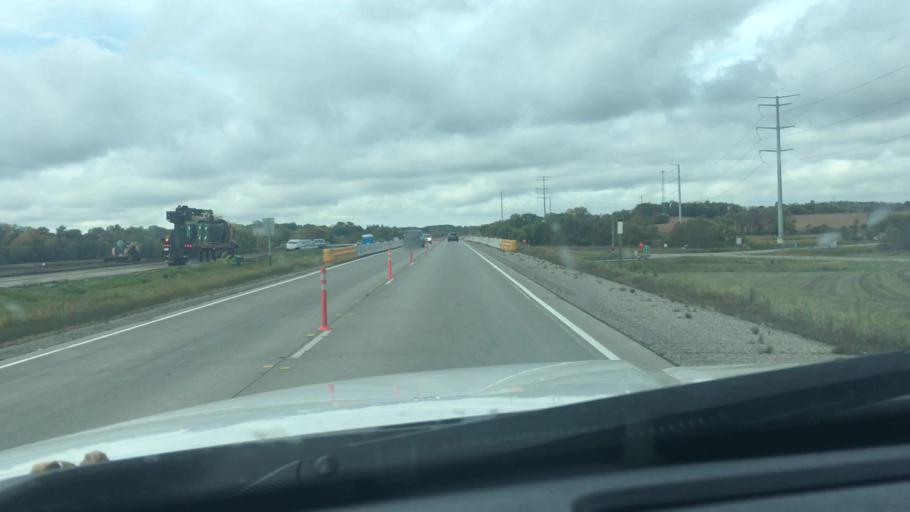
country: US
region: Minnesota
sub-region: Douglas County
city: Alexandria
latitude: 45.8811
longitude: -95.4875
